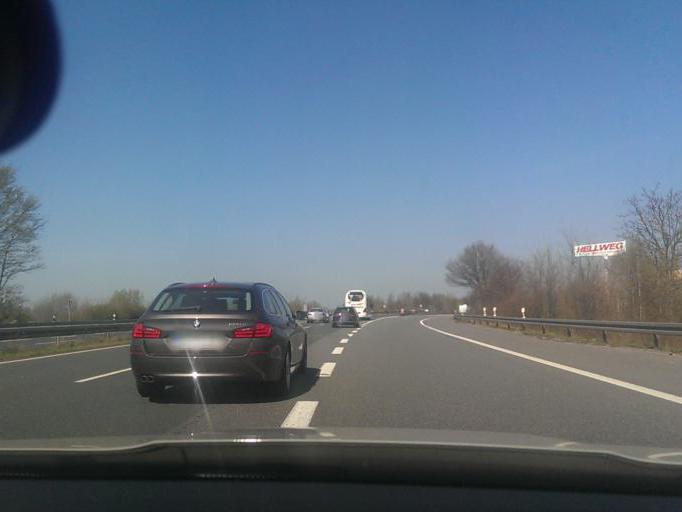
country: DE
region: Lower Saxony
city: Langenhagen
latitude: 52.4433
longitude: 9.7198
